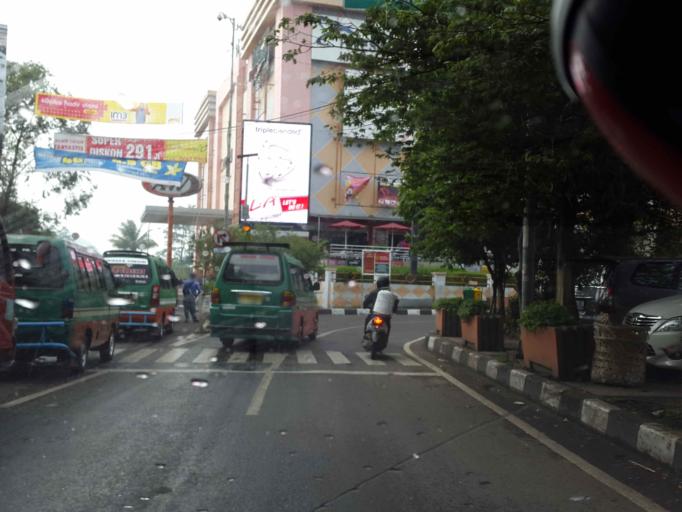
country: ID
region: West Java
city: Cimahi
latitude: -6.8791
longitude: 107.5402
